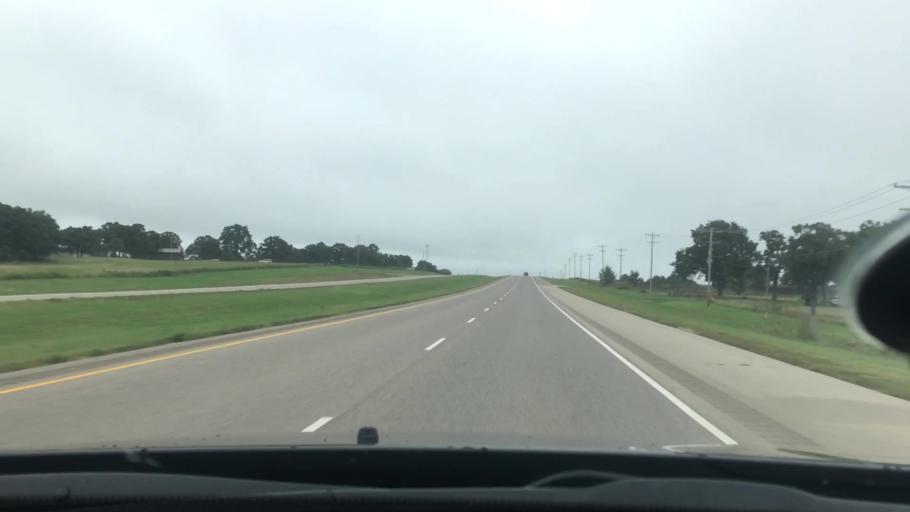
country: US
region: Oklahoma
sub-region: Lincoln County
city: Prague
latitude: 35.3649
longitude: -96.6715
